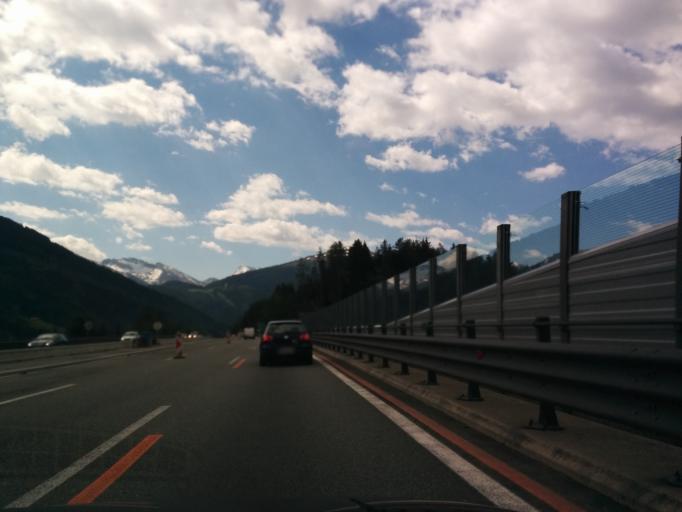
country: AT
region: Tyrol
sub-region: Politischer Bezirk Innsbruck Land
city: Gries am Brenner
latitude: 47.0574
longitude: 11.4801
